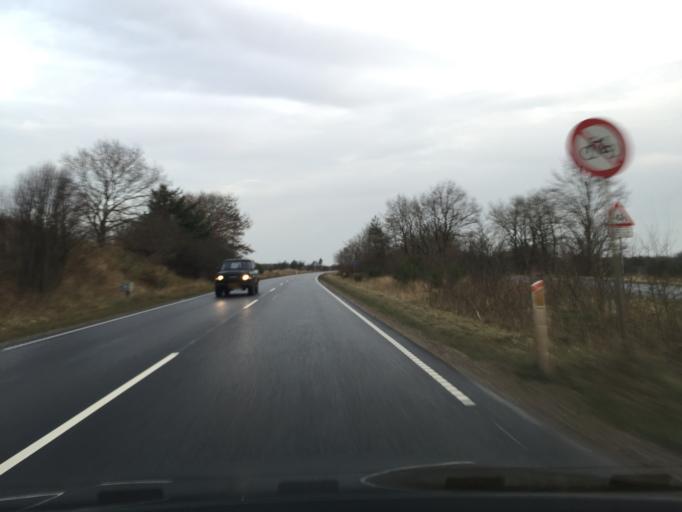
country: DK
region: Central Jutland
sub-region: Viborg Kommune
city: Bjerringbro
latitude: 56.3667
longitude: 9.6127
